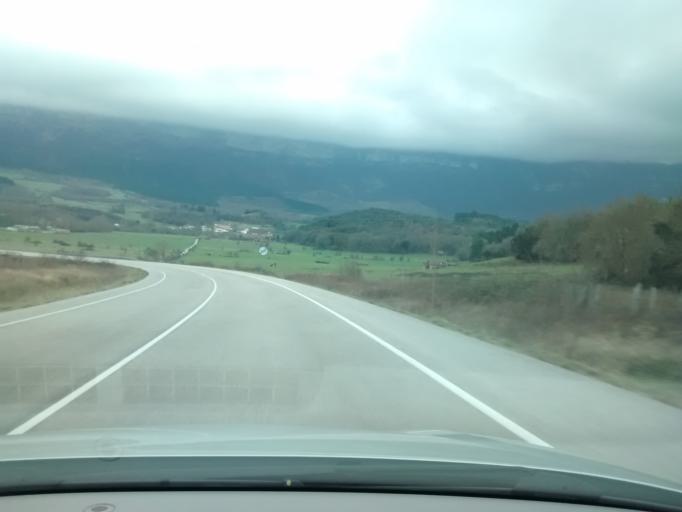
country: ES
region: Castille and Leon
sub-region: Provincia de Burgos
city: Villasana de Mena
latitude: 43.0970
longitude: -3.3067
